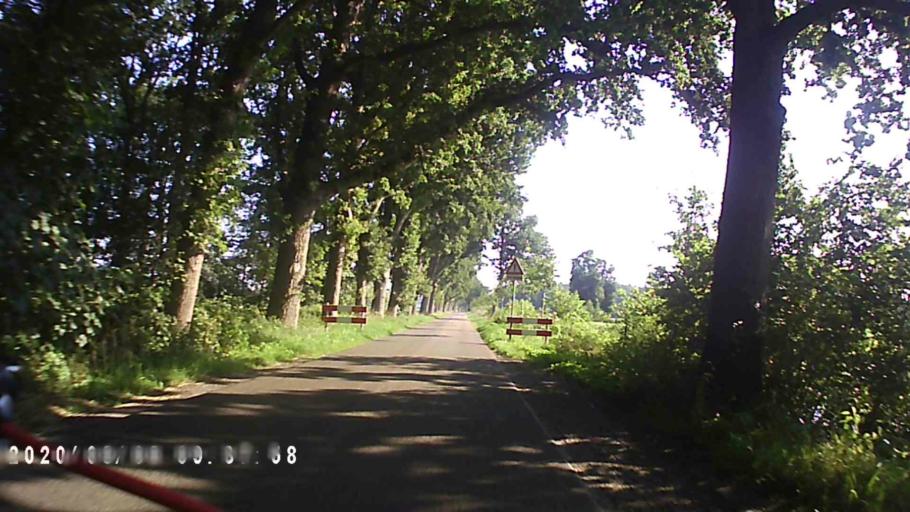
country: NL
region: Groningen
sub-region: Gemeente Leek
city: Leek
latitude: 53.0529
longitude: 6.3880
